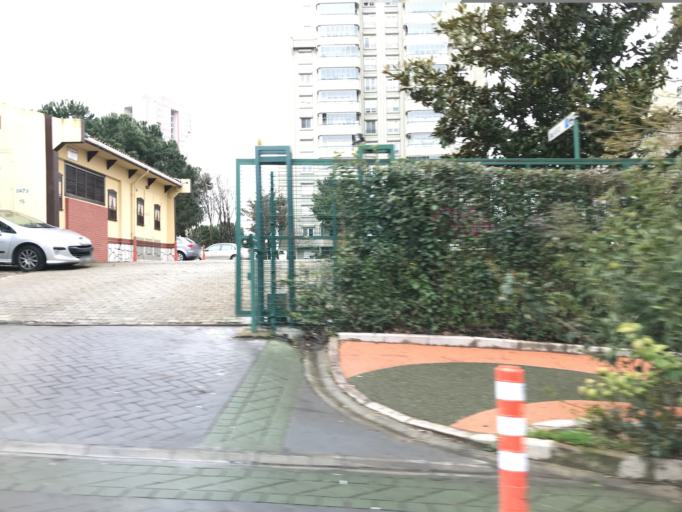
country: TR
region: Istanbul
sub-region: Atasehir
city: Atasehir
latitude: 40.9912
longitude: 29.1203
